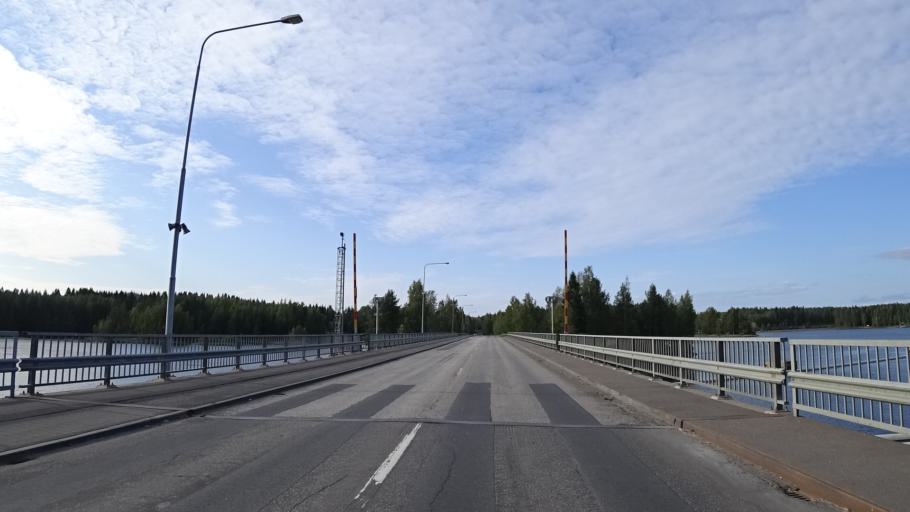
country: FI
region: North Karelia
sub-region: Joensuu
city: Eno
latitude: 62.8022
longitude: 30.1536
